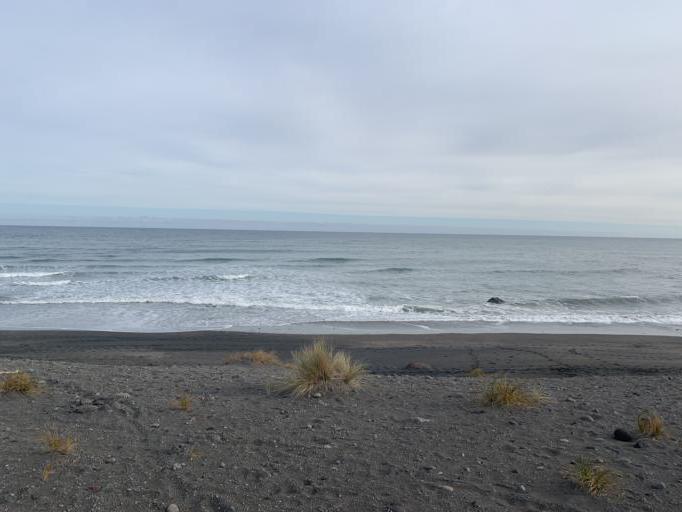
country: NZ
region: Taranaki
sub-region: South Taranaki District
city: Hawera
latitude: -39.5662
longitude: 174.0586
